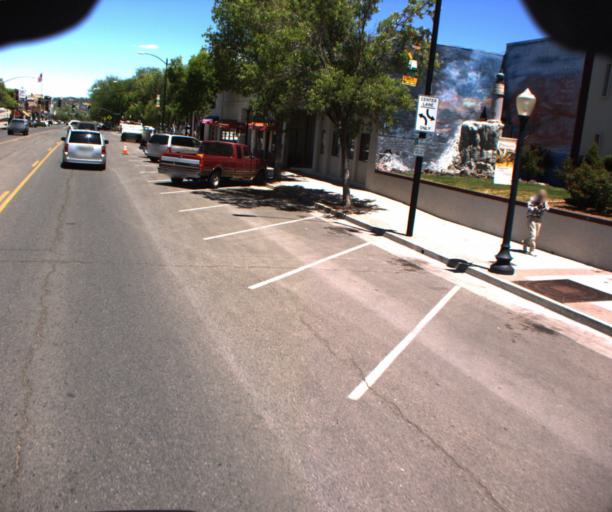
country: US
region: Arizona
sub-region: Yavapai County
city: Prescott
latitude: 34.5385
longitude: -112.4702
